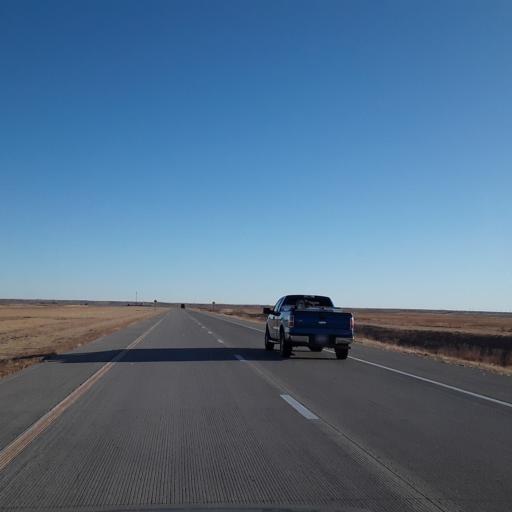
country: US
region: Kansas
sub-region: Seward County
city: Liberal
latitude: 37.1092
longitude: -100.7849
